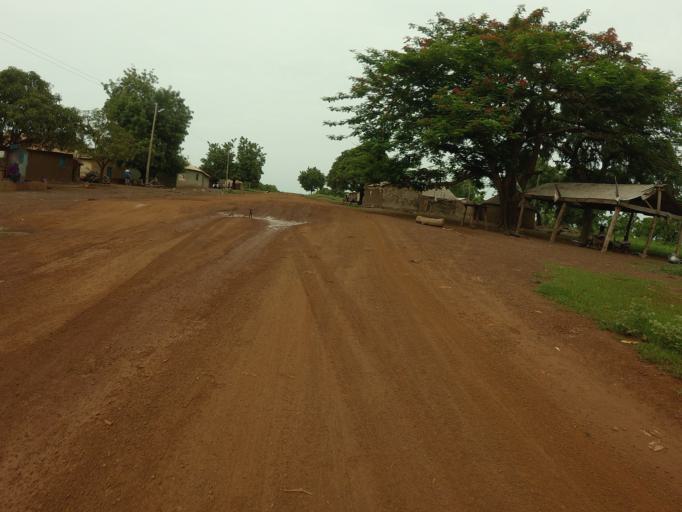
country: GH
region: Northern
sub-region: Yendi
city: Yendi
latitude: 9.0346
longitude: -0.0131
